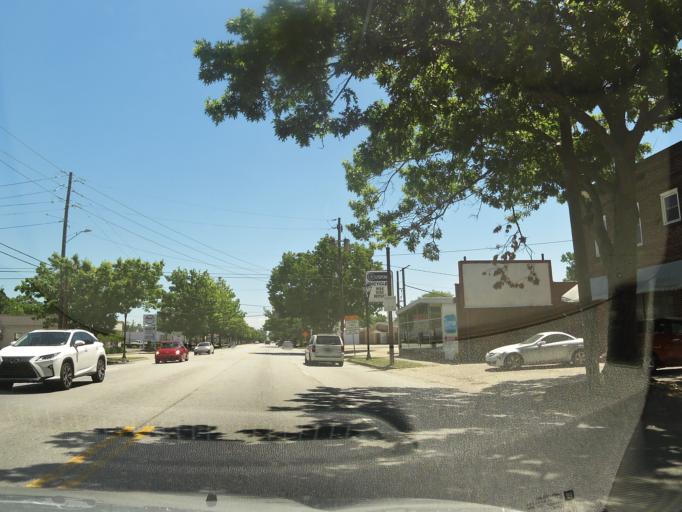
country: US
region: Georgia
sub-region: Richmond County
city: Augusta
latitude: 33.4757
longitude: -82.0007
